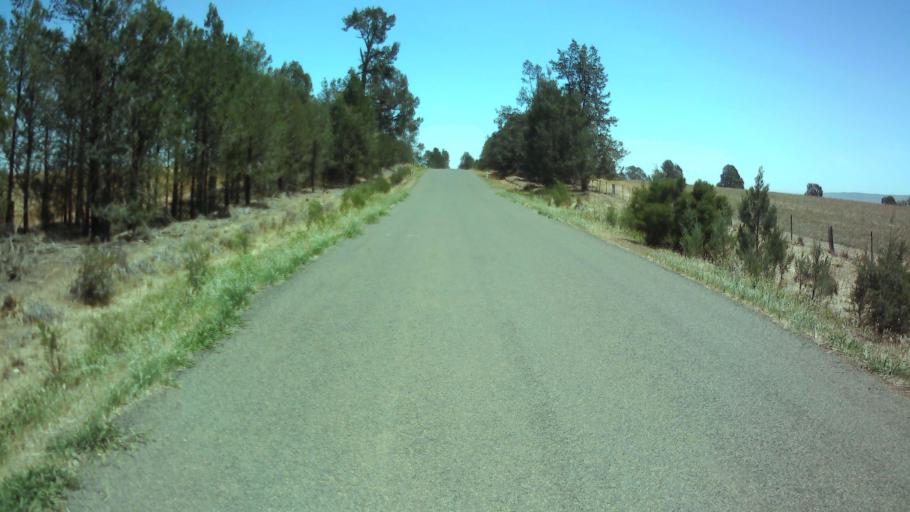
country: AU
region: New South Wales
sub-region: Weddin
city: Grenfell
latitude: -34.0504
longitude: 148.1930
